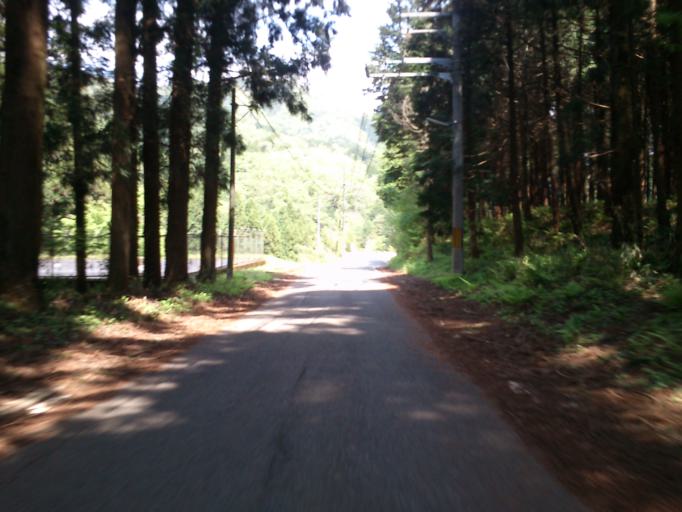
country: JP
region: Kyoto
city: Fukuchiyama
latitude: 35.3412
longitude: 134.9243
